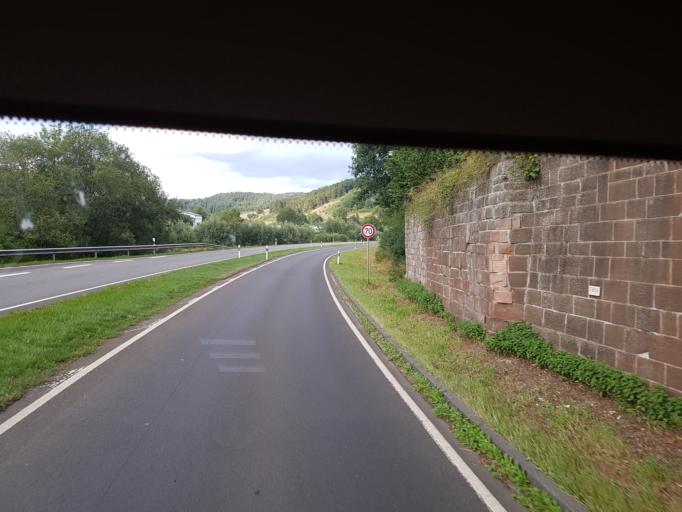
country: DE
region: Rheinland-Pfalz
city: Rockeskyll
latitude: 50.2457
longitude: 6.6932
